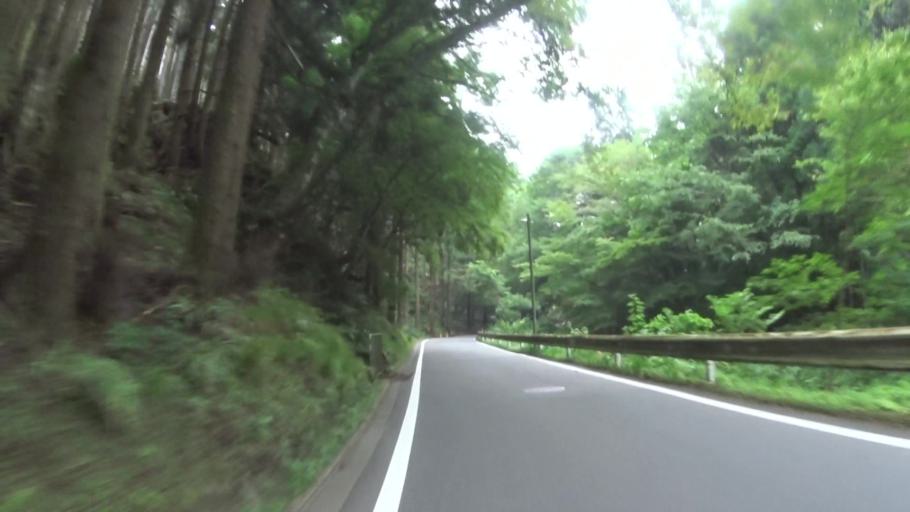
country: JP
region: Kyoto
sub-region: Kyoto-shi
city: Kamigyo-ku
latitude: 35.1141
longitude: 135.7603
